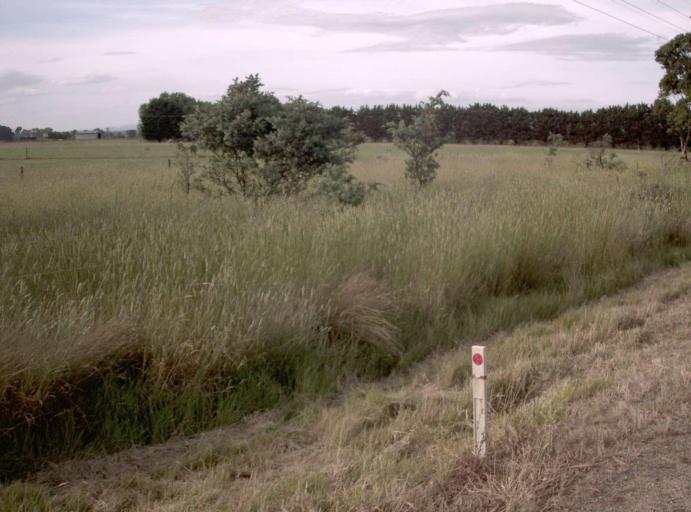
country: AU
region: Victoria
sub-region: Wellington
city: Heyfield
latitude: -38.0127
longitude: 146.7754
